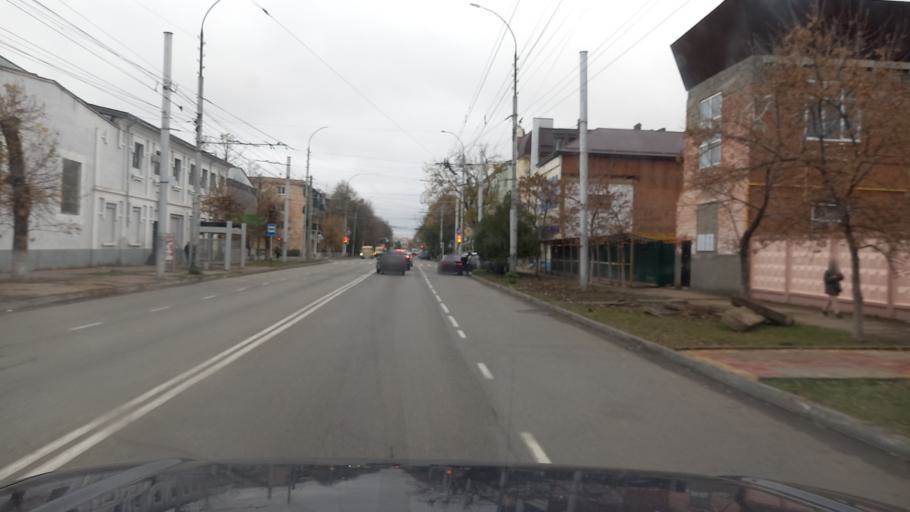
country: RU
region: Adygeya
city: Maykop
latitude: 44.6146
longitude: 40.1087
